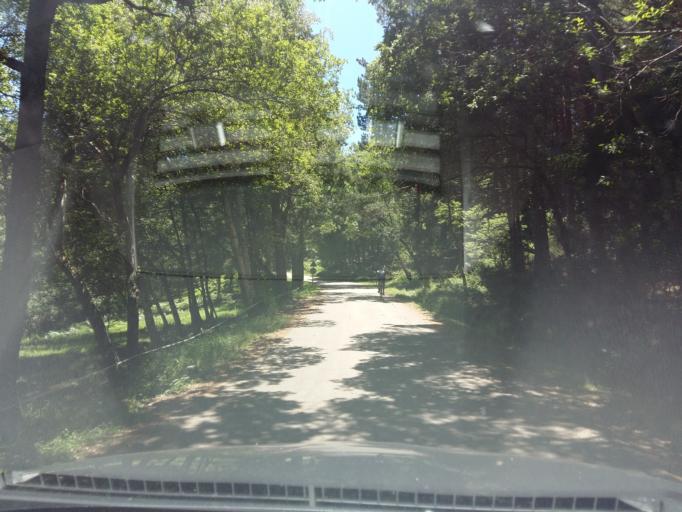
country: ES
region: Castille and Leon
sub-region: Provincia de Soria
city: Vozmediano
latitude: 41.8159
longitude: -1.8221
